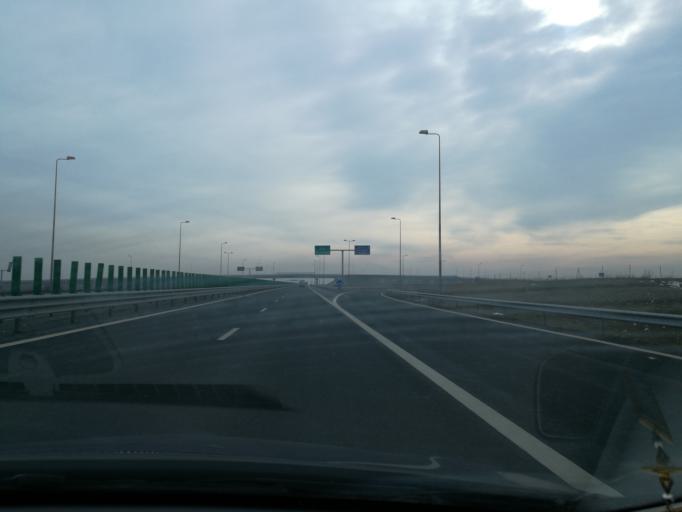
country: RO
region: Constanta
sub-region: Municipiul Medgidia
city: Valea Dacilor
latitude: 44.1774
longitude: 28.3186
